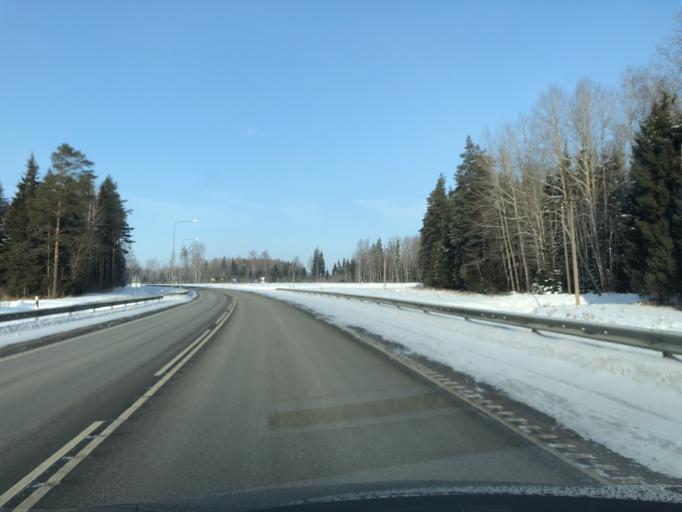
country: EE
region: Tartu
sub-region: Tartu linn
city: Tartu
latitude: 58.4065
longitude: 26.6527
